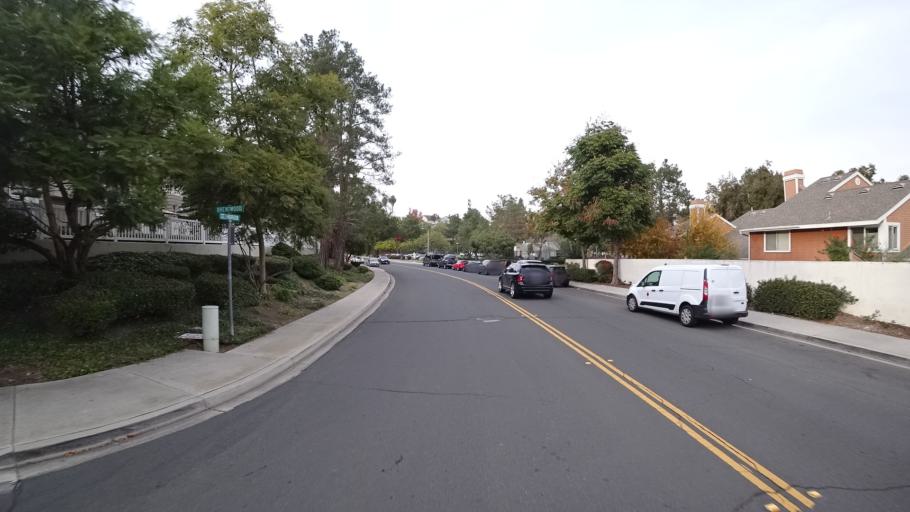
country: US
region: California
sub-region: Orange County
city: Laguna Woods
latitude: 33.5924
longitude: -117.7207
